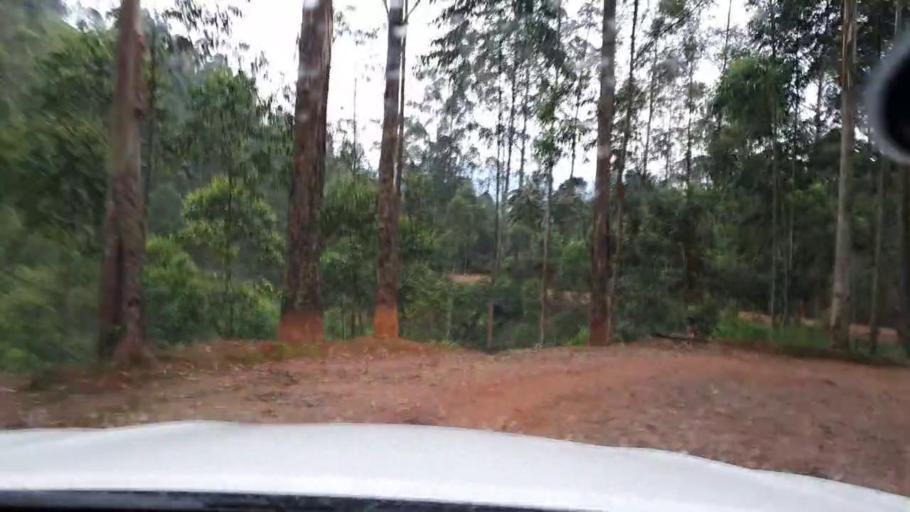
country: RW
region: Western Province
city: Cyangugu
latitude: -2.4089
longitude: 29.2026
